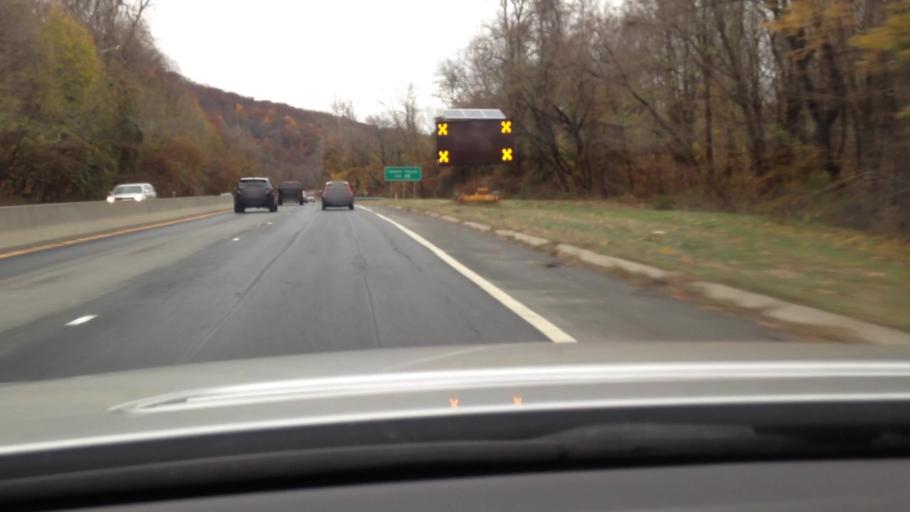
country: US
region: New York
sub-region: Westchester County
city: Elmsford
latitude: 41.0871
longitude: -73.8222
